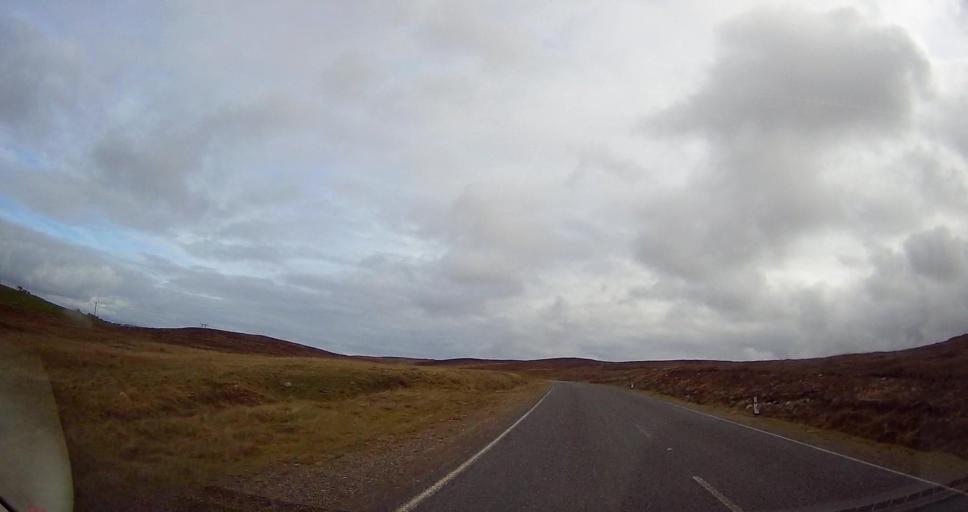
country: GB
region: Scotland
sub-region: Shetland Islands
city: Shetland
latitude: 60.5730
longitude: -1.1721
